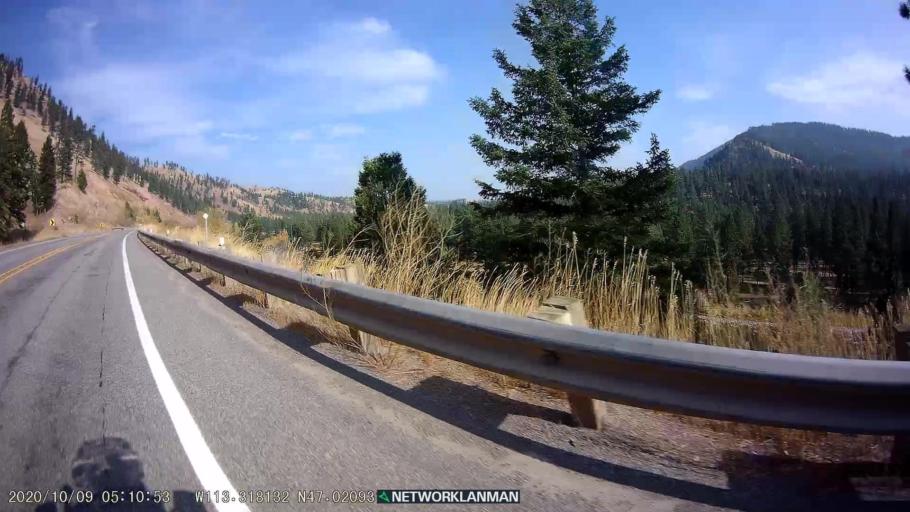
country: US
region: Montana
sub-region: Missoula County
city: Seeley Lake
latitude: 47.0212
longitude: -113.3182
